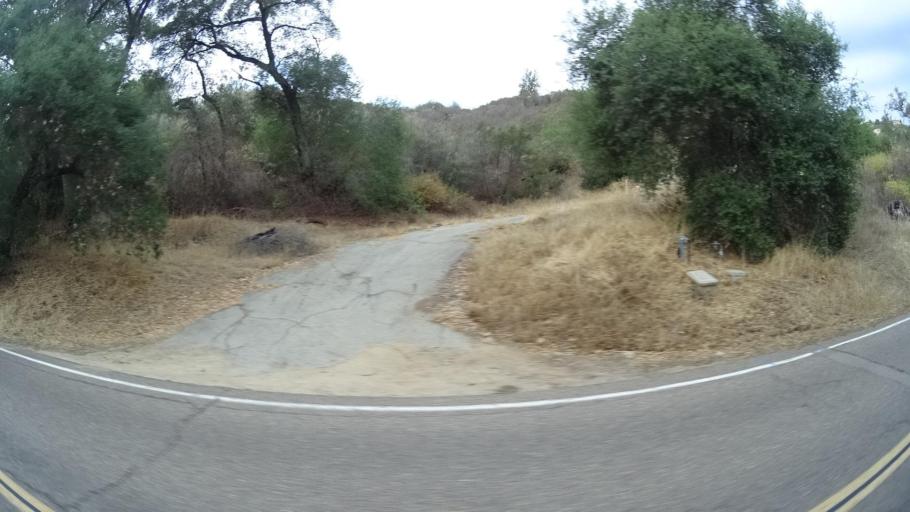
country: US
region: California
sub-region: San Diego County
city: Ramona
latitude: 32.9829
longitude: -116.9236
